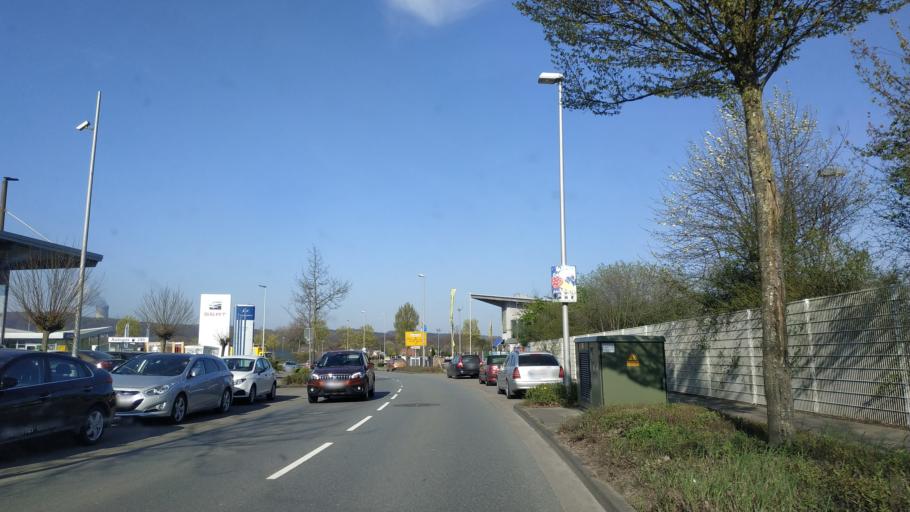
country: DE
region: North Rhine-Westphalia
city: Ibbenburen
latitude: 52.2586
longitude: 7.7257
